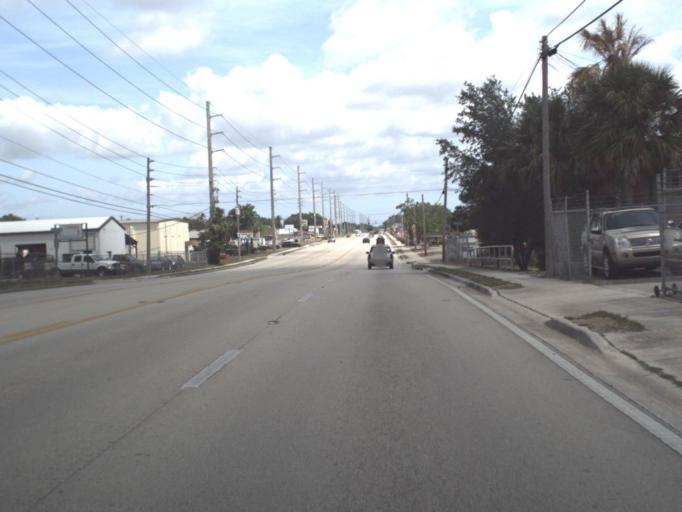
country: US
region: Florida
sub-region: Brevard County
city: Cocoa
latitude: 28.3775
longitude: -80.7550
